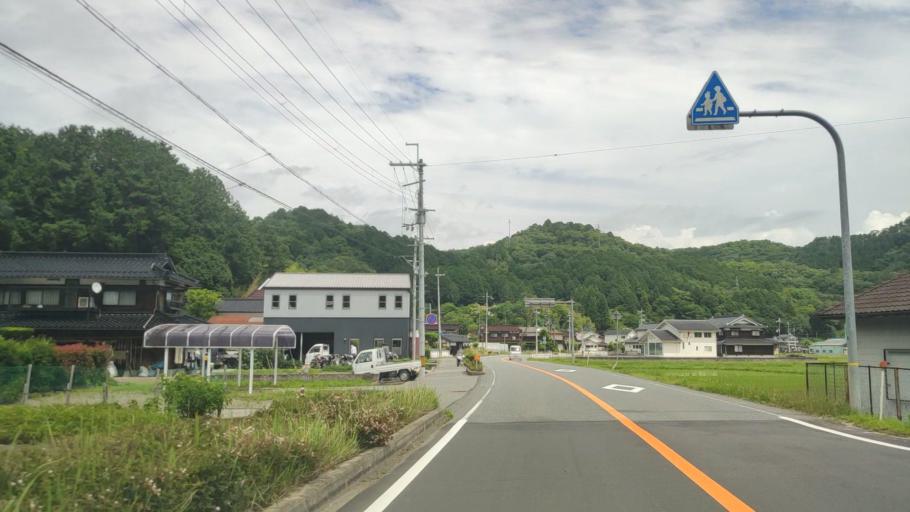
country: JP
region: Hyogo
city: Yamazakicho-nakabirose
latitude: 35.0296
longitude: 134.3672
